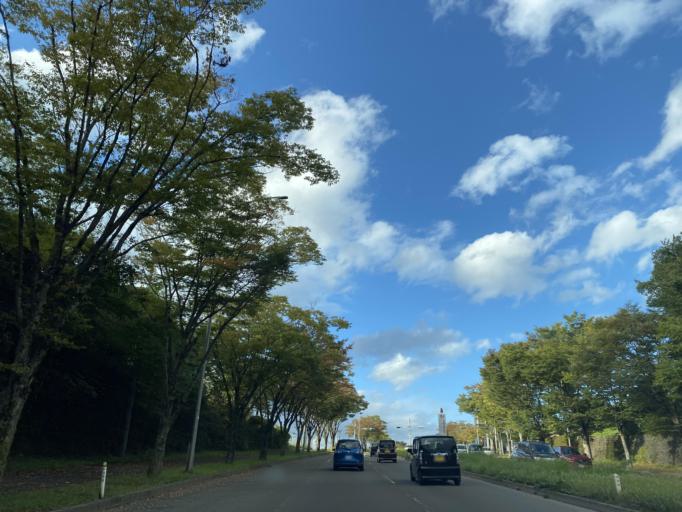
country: JP
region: Miyagi
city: Sendai-shi
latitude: 38.3293
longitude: 140.8411
